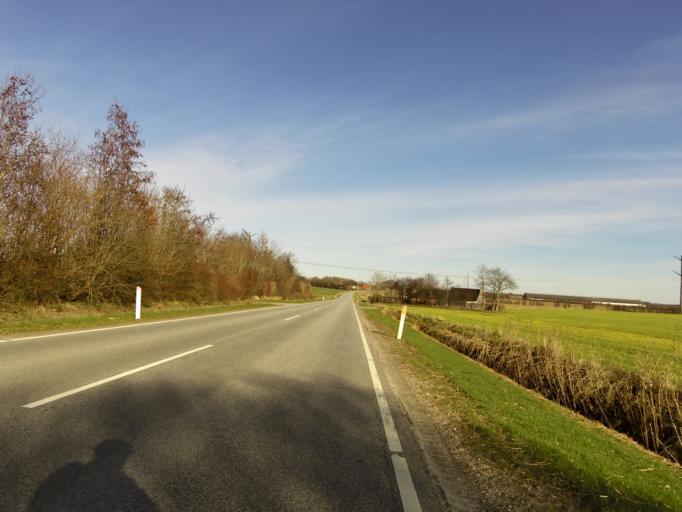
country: DK
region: South Denmark
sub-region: Vejen Kommune
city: Rodding
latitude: 55.3579
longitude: 9.1600
